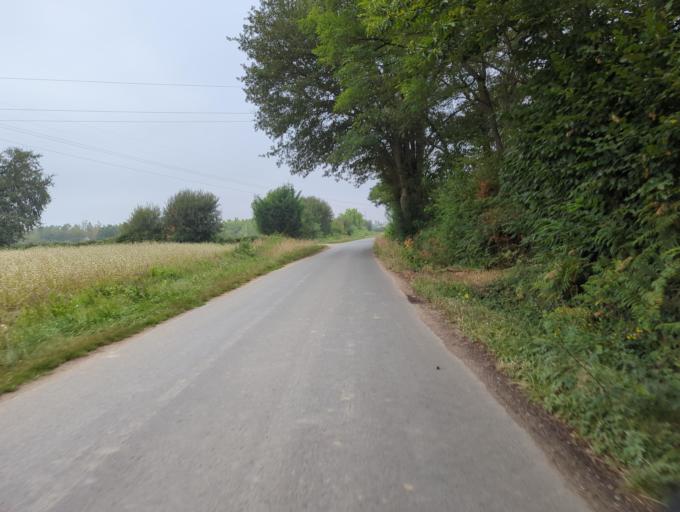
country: FR
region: Pays de la Loire
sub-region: Departement de Maine-et-Loire
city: Trelaze
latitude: 47.4792
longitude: -0.4646
